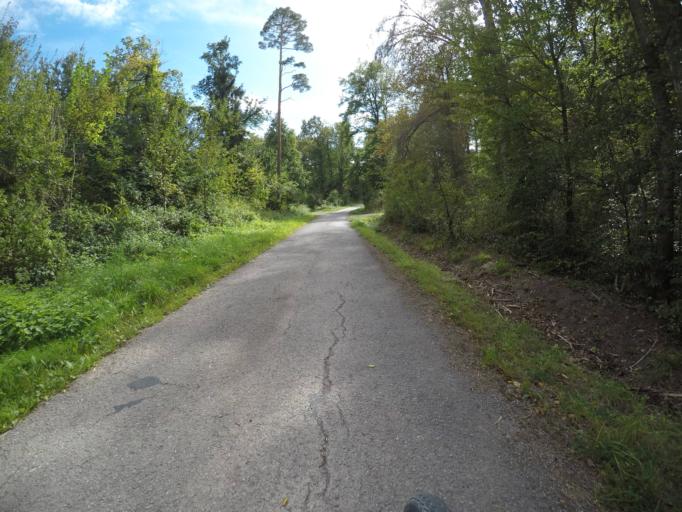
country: DE
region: Baden-Wuerttemberg
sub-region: Karlsruhe Region
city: Sternenfels
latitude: 48.9980
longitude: 8.8578
